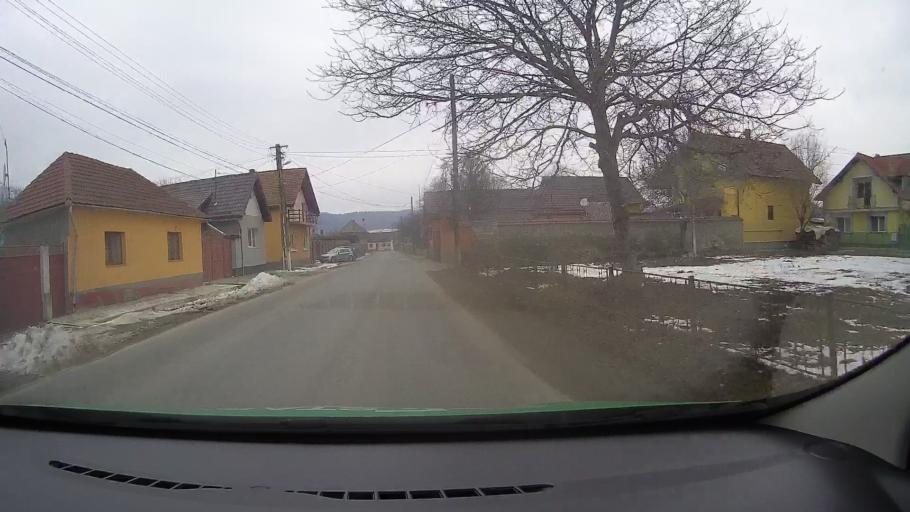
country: RO
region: Brasov
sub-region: Comuna Vulcan
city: Vulcan
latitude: 45.6345
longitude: 25.4255
